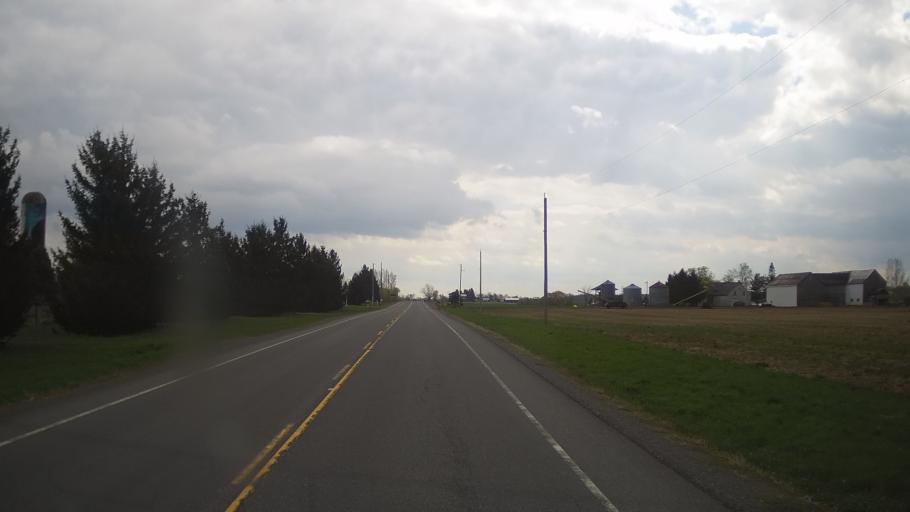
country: CA
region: Ontario
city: Hawkesbury
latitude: 45.5405
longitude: -74.5506
